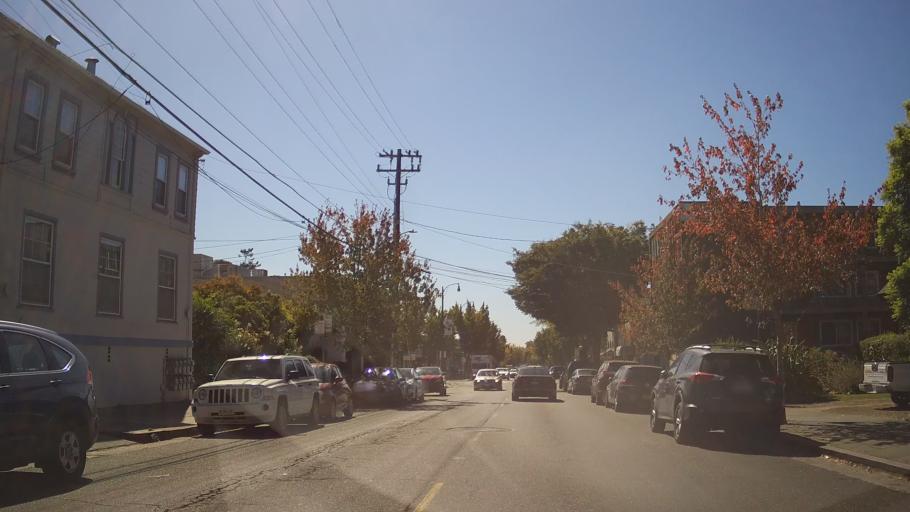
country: US
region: California
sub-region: Alameda County
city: Berkeley
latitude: 37.8593
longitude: -122.2533
